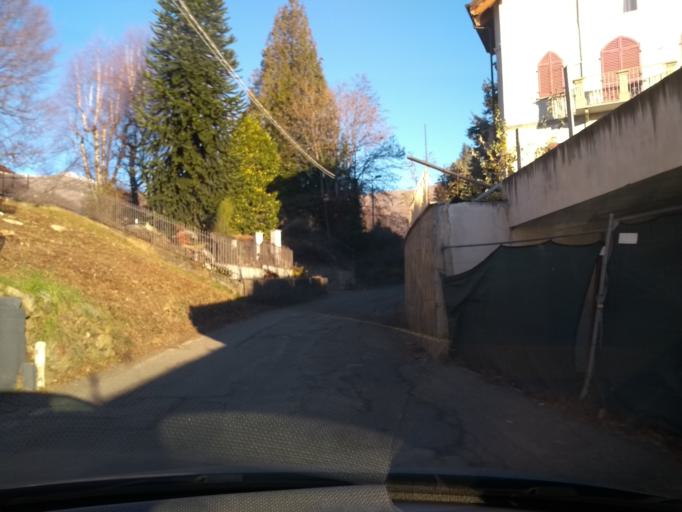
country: IT
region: Piedmont
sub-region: Provincia di Torino
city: Corio
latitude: 45.3144
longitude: 7.5300
